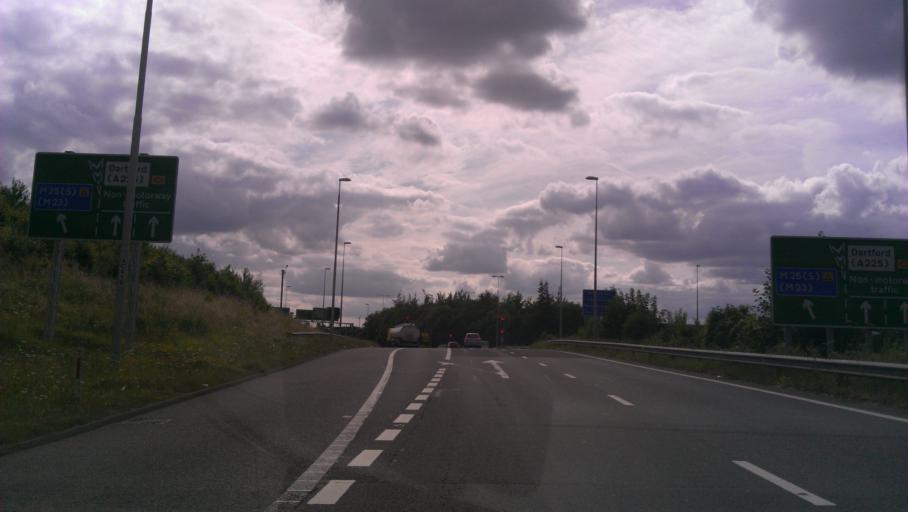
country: GB
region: England
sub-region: Kent
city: Dartford
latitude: 51.4266
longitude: 0.2420
